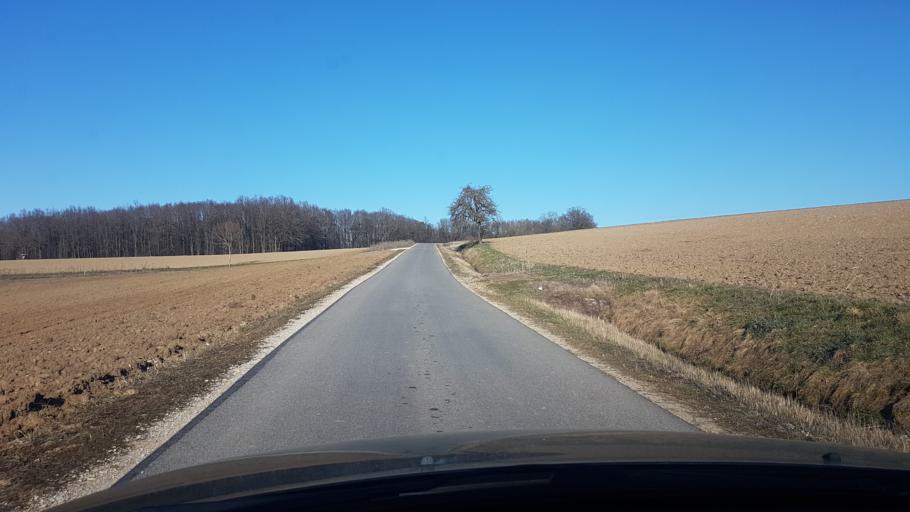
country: DE
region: Bavaria
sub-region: Upper Franconia
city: Zapfendorf
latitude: 50.0171
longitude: 10.9850
